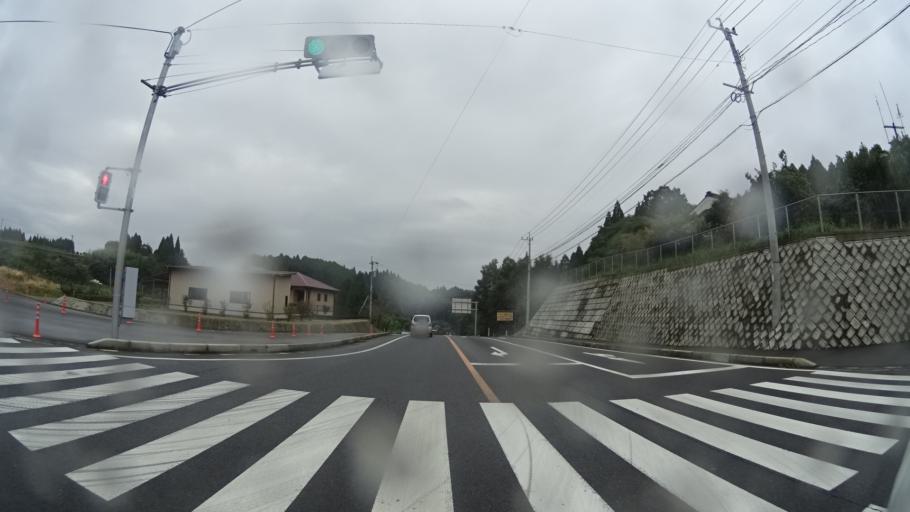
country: JP
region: Kagoshima
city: Kajiki
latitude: 31.8120
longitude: 130.6774
